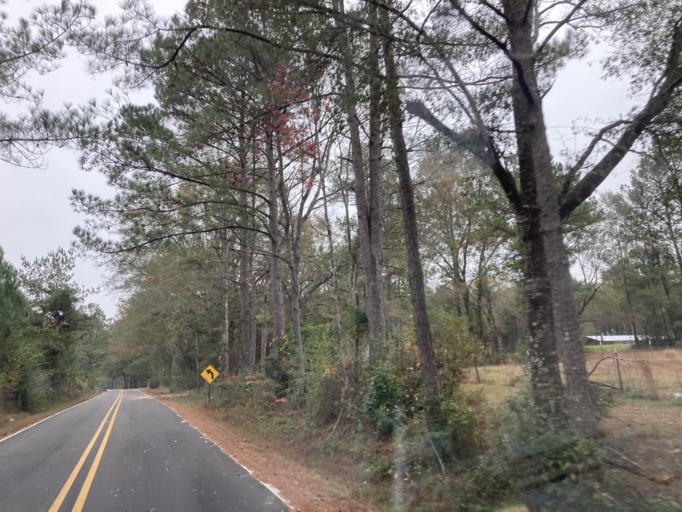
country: US
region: Mississippi
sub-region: Lamar County
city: Lumberton
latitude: 31.0650
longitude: -89.4197
